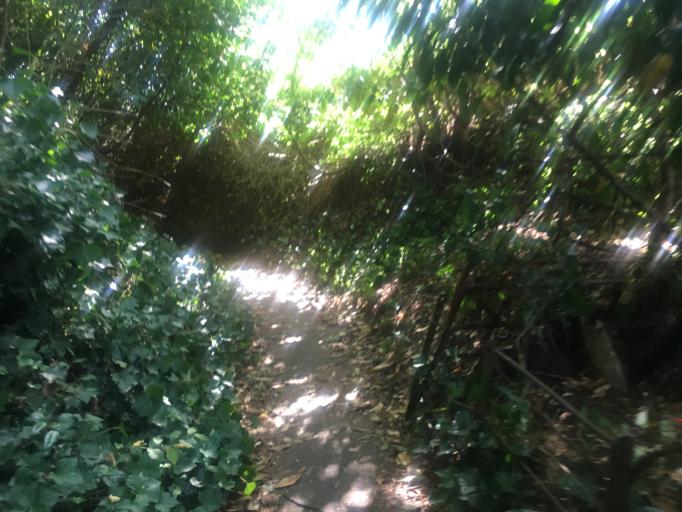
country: GB
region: England
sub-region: Surrey
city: Reigate
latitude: 51.2302
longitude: -0.2025
